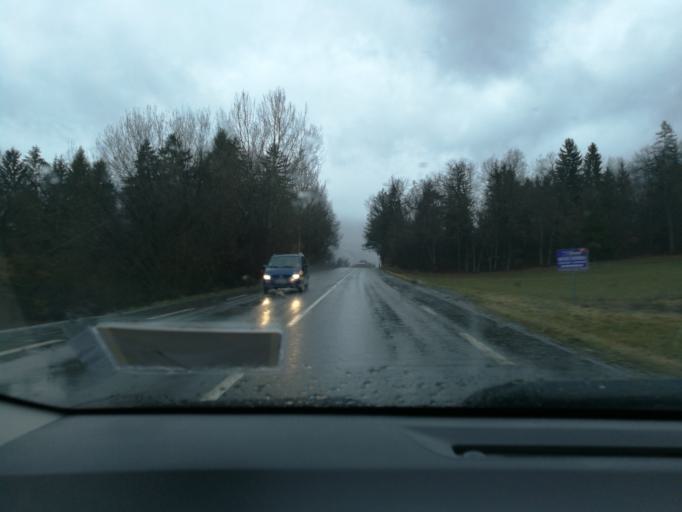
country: FR
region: Rhone-Alpes
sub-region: Departement de la Haute-Savoie
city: Domancy
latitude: 45.9262
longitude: 6.6576
